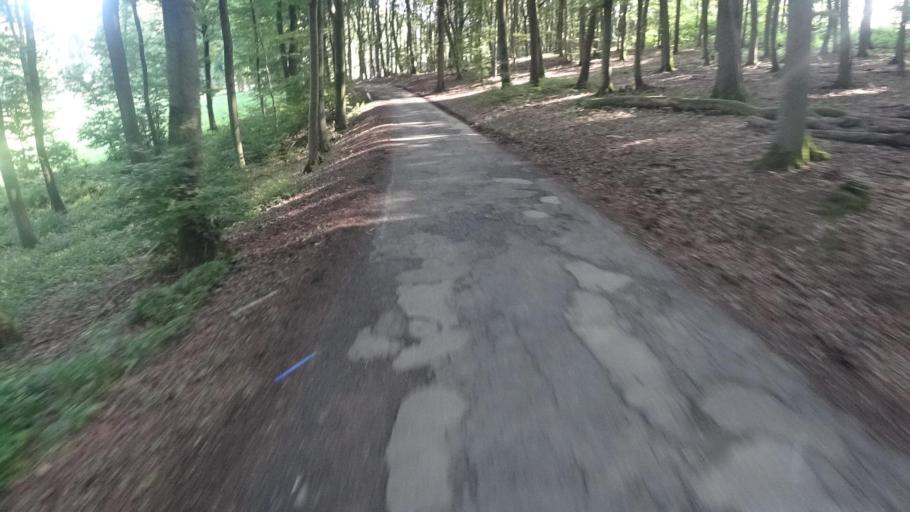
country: DE
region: Rheinland-Pfalz
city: Sankt Katharinen
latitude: 50.5617
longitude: 7.3694
